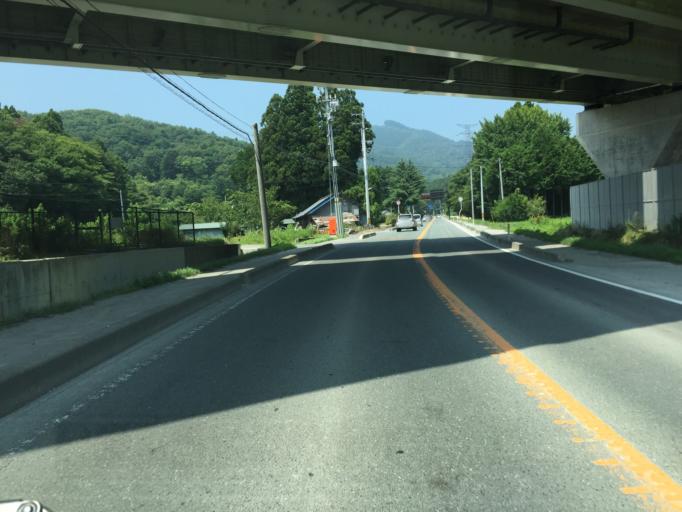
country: JP
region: Miyagi
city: Marumori
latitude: 37.8491
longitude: 140.8799
